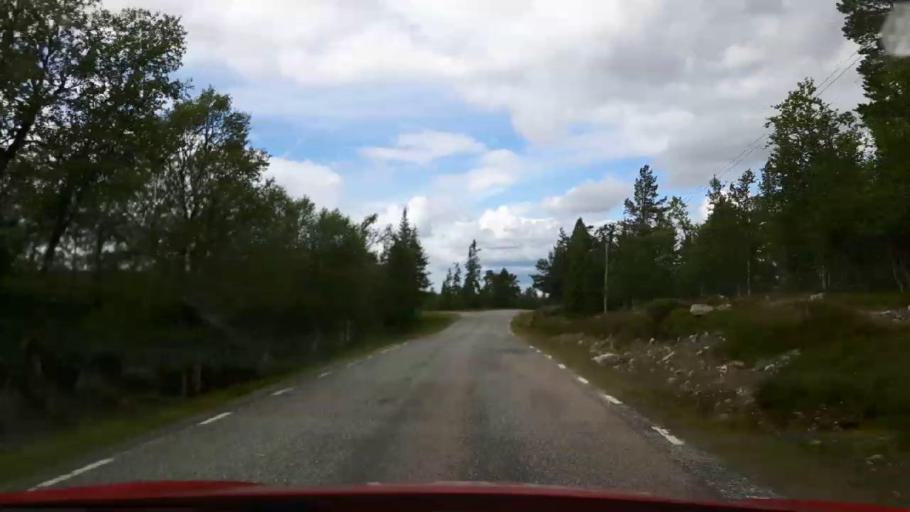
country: NO
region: Hedmark
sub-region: Engerdal
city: Engerdal
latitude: 62.3358
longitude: 12.8009
